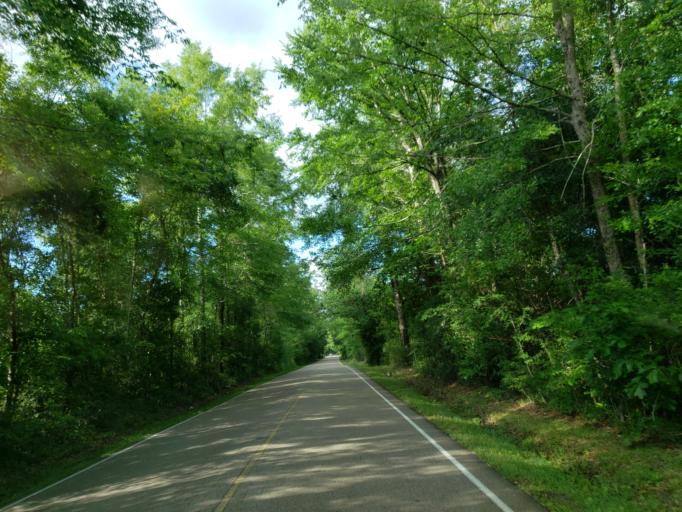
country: US
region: Mississippi
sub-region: Forrest County
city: Hattiesburg
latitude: 31.2527
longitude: -89.2392
